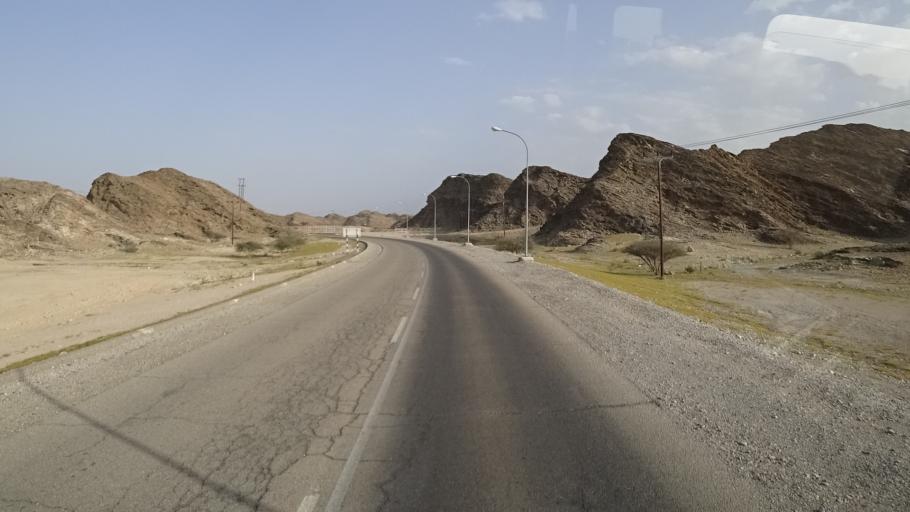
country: OM
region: Muhafazat Masqat
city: Bawshar
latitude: 23.3726
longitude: 58.5177
